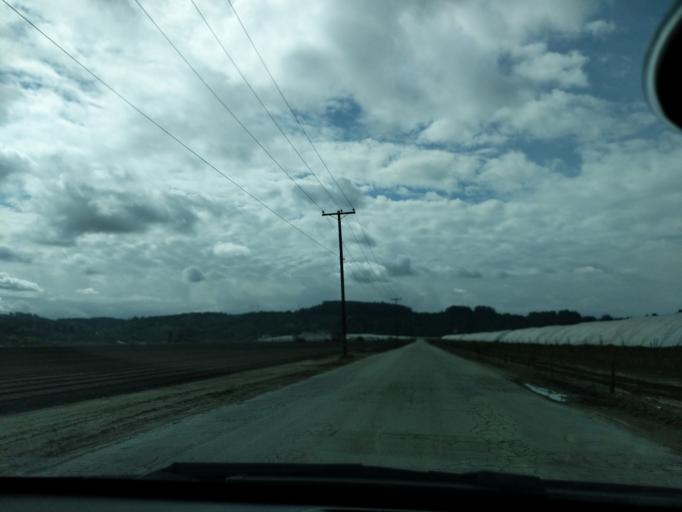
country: US
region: California
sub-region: San Benito County
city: Aromas
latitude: 36.9016
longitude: -121.6762
